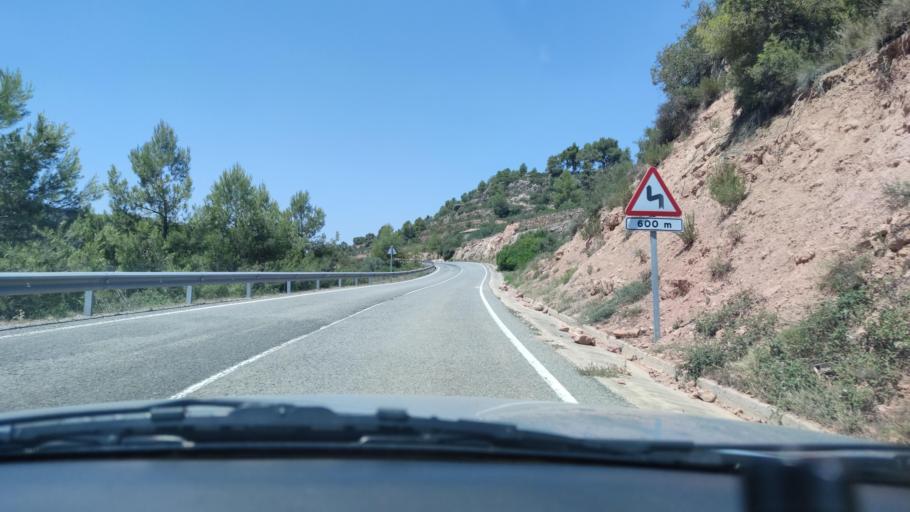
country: ES
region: Catalonia
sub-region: Provincia de Lleida
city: Juncosa
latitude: 41.3986
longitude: 0.7159
